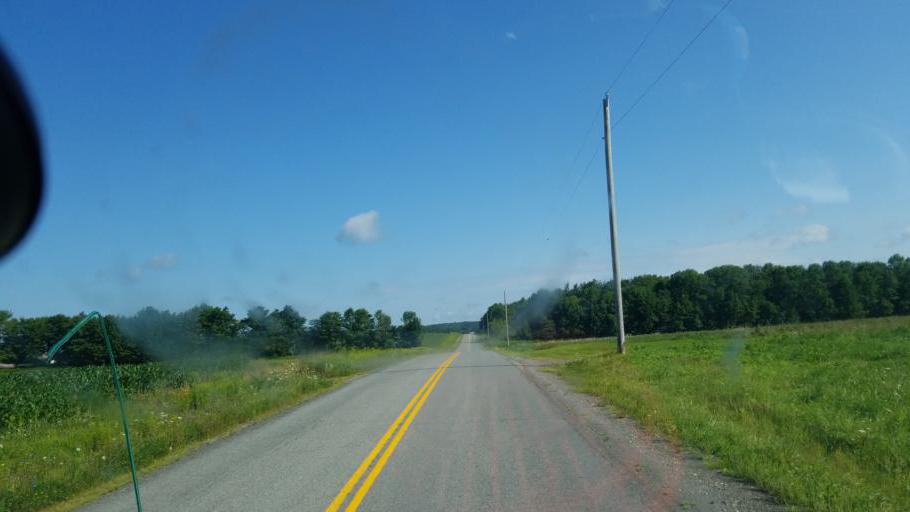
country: US
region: New York
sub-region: Allegany County
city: Andover
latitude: 42.1711
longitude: -77.7129
